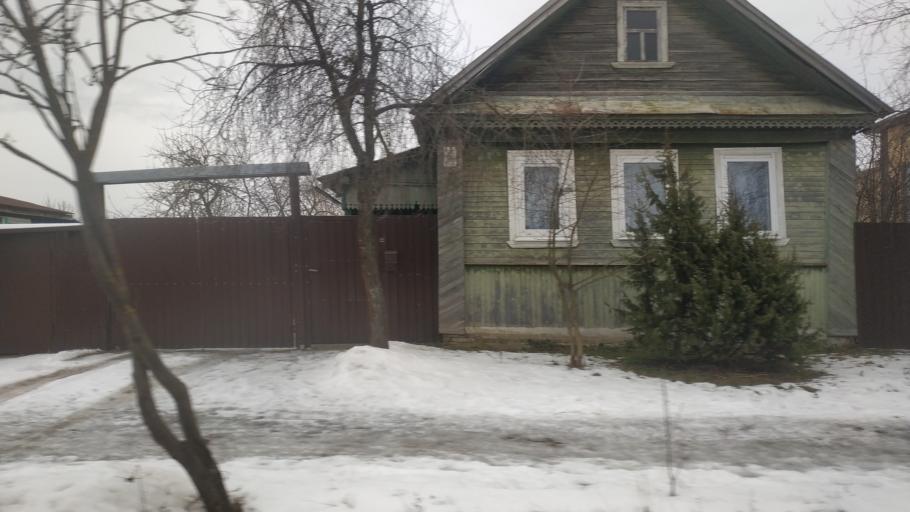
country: RU
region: Tverskaya
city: Tver
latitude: 56.8859
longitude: 35.8966
